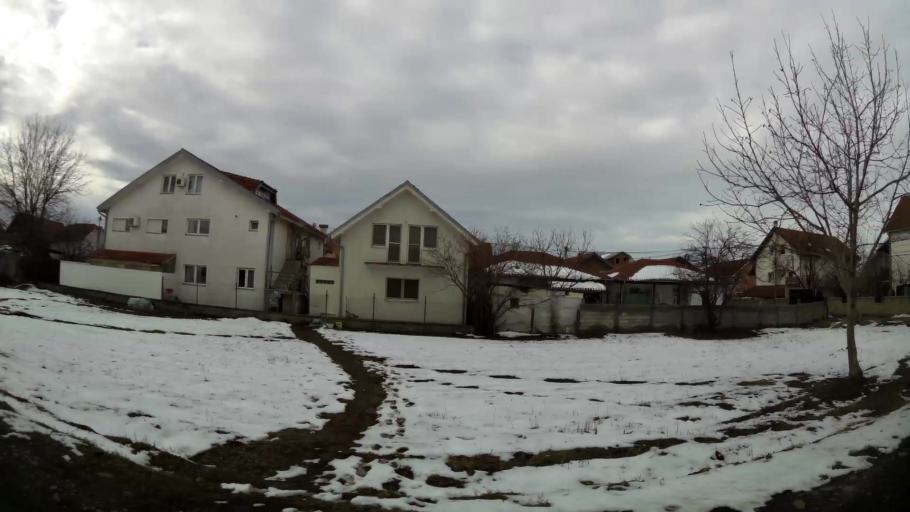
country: RS
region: Central Serbia
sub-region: Belgrade
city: Surcin
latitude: 44.8041
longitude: 20.3345
